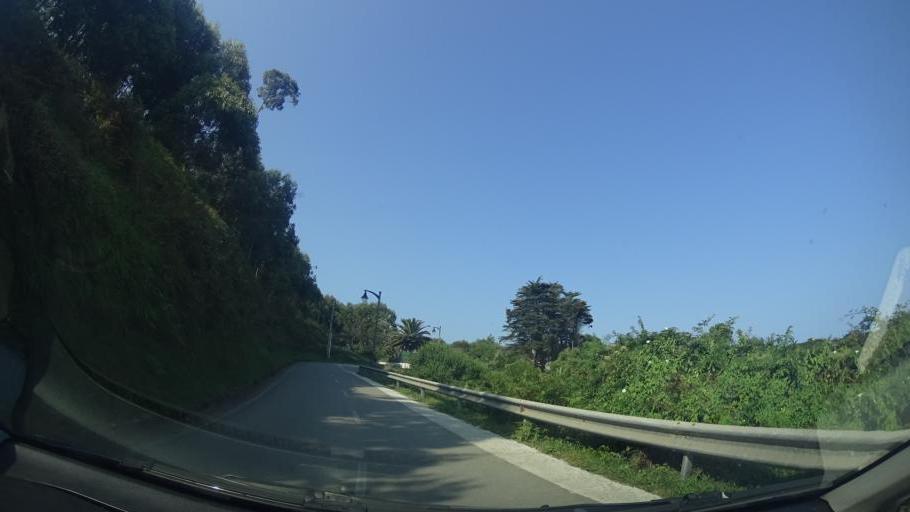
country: ES
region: Asturias
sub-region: Province of Asturias
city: Colunga
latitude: 43.4743
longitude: -5.1780
